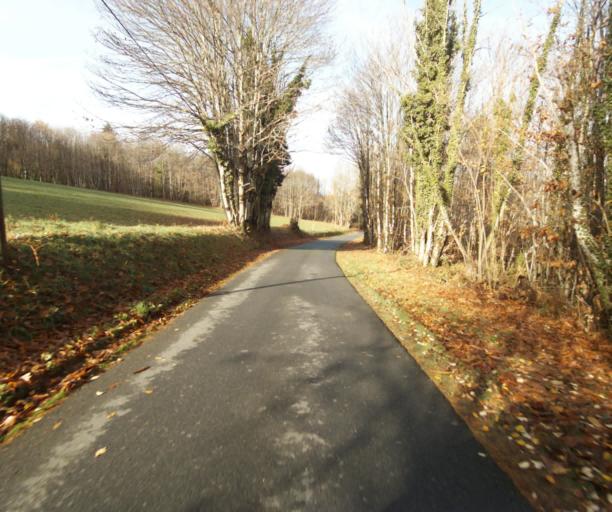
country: FR
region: Limousin
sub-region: Departement de la Correze
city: Sainte-Fortunade
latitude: 45.2172
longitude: 1.7511
